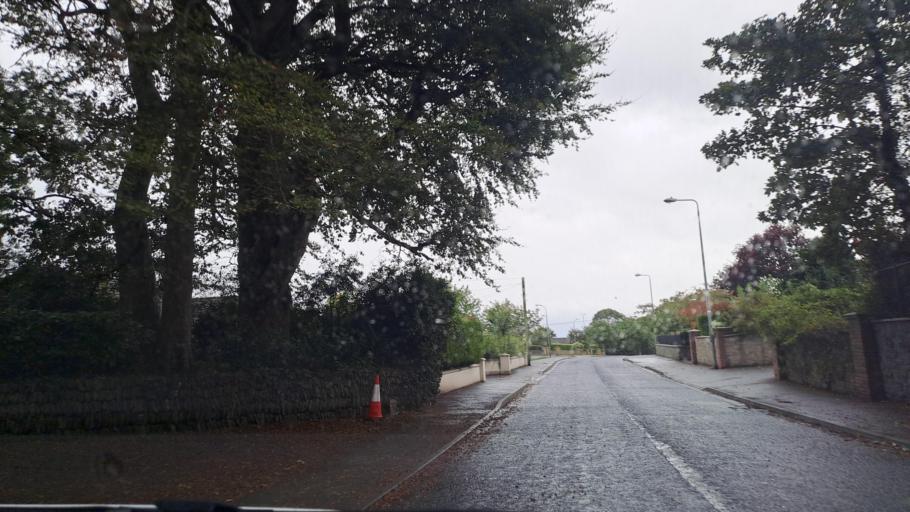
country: IE
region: Leinster
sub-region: Lu
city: Blackrock
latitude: 53.9590
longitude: -6.3756
